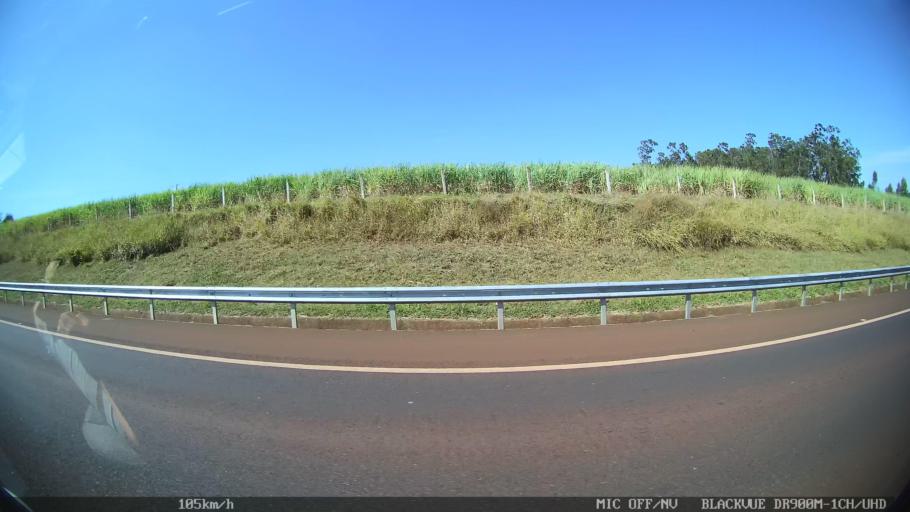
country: BR
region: Sao Paulo
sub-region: Franca
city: Franca
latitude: -20.6259
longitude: -47.4628
